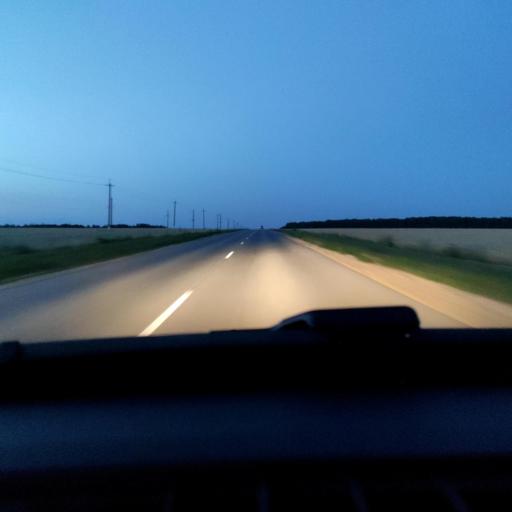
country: RU
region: Lipetsk
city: Zadonsk
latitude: 52.3032
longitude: 38.8654
